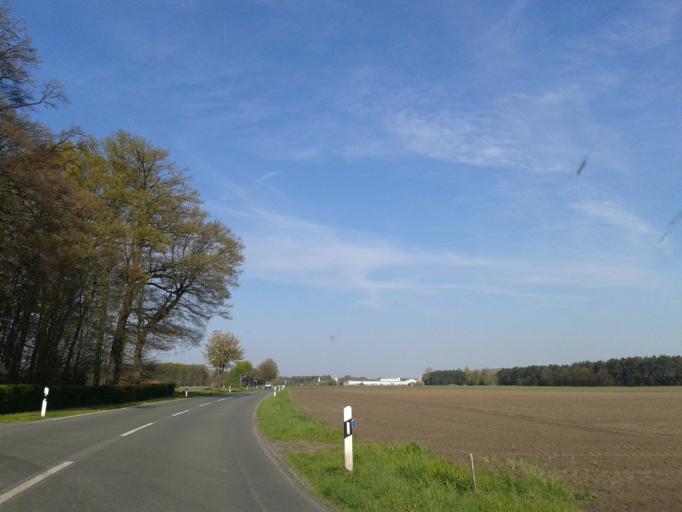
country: DE
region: North Rhine-Westphalia
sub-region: Regierungsbezirk Detmold
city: Delbruck
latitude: 51.7202
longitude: 8.5269
